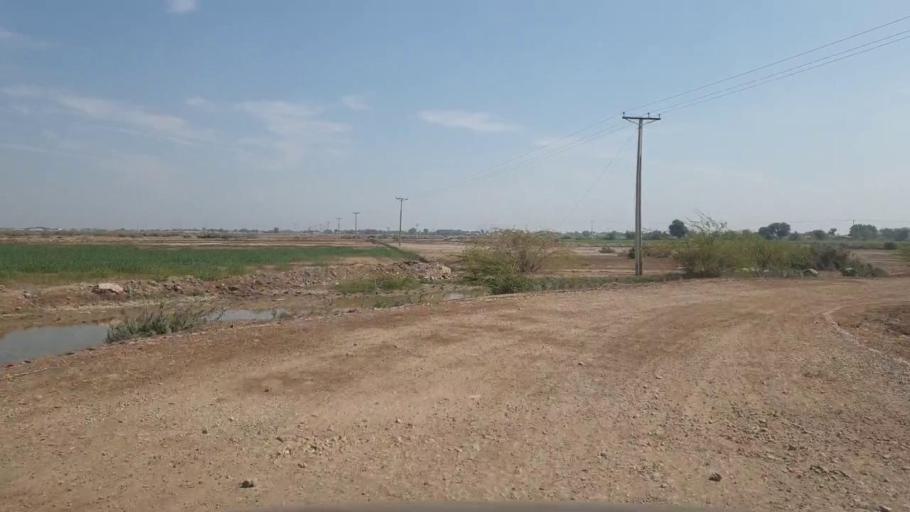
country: PK
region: Sindh
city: Mirwah Gorchani
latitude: 25.4361
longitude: 69.1957
